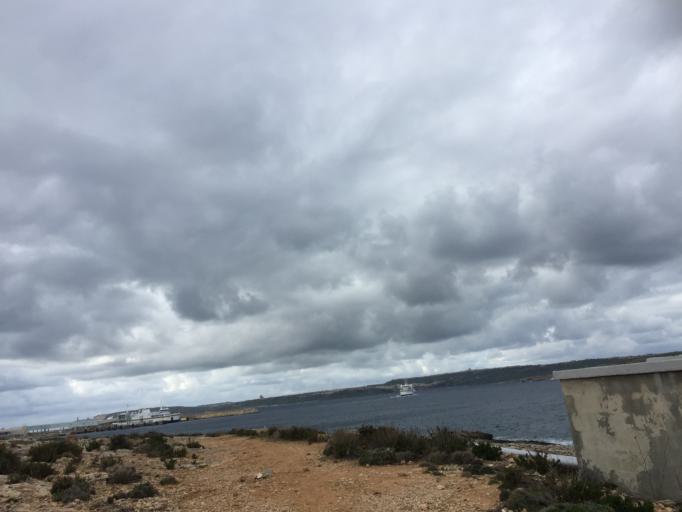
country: MT
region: Il-Mellieha
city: Mellieha
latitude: 35.9867
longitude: 14.3367
